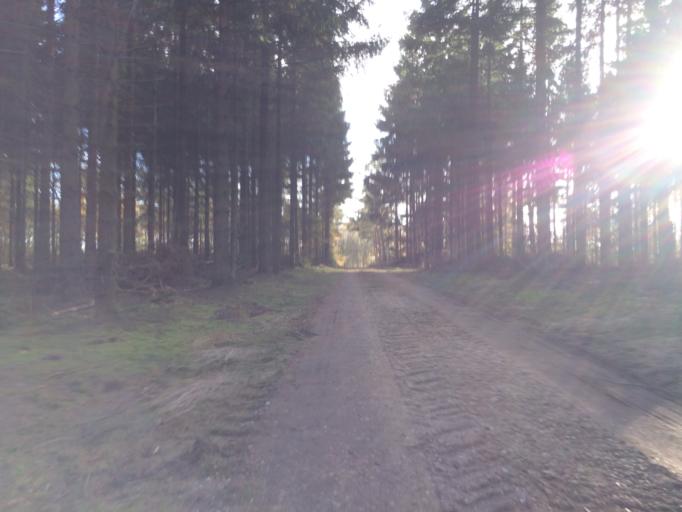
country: DK
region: Central Jutland
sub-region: Holstebro Kommune
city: Ulfborg
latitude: 56.2066
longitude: 8.4665
